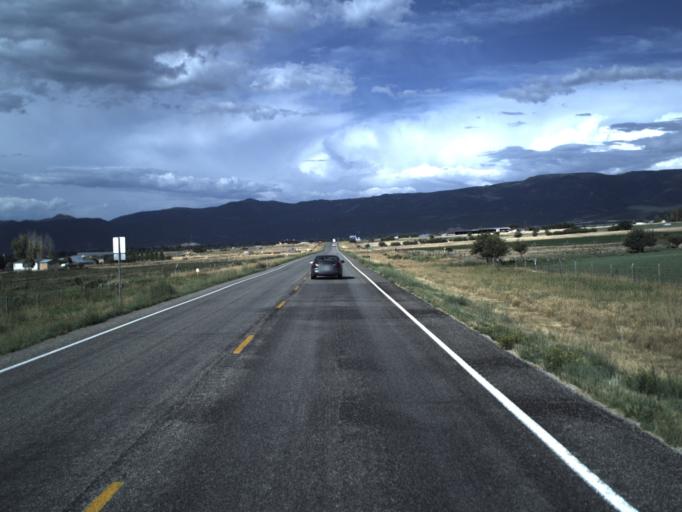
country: US
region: Utah
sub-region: Sanpete County
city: Mount Pleasant
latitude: 39.5159
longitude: -111.4888
